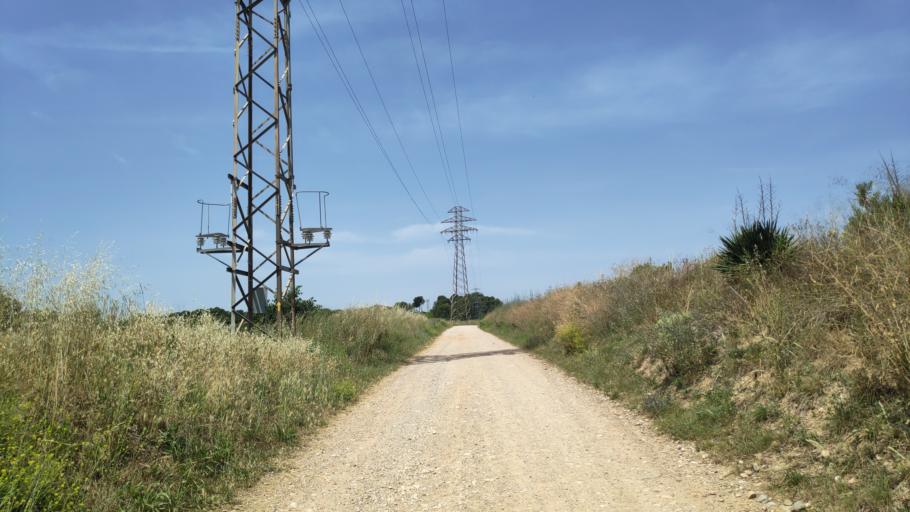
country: ES
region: Catalonia
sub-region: Provincia de Barcelona
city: Terrassa
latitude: 41.5654
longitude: 2.0575
